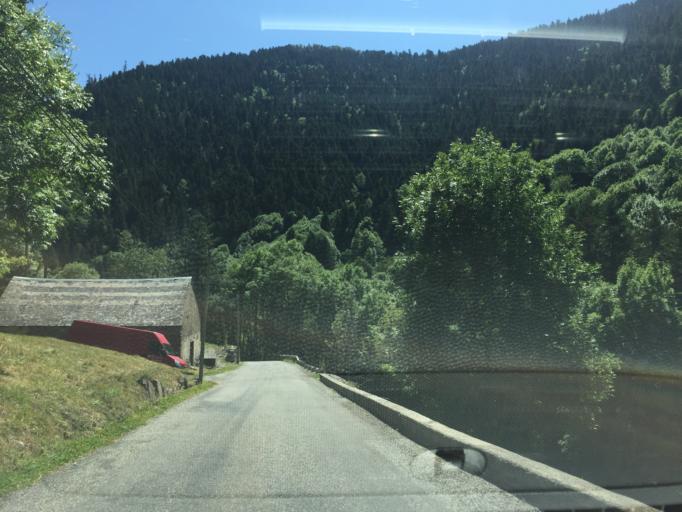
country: FR
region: Midi-Pyrenees
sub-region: Departement des Hautes-Pyrenees
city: Saint-Lary-Soulan
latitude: 42.8486
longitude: 0.2970
